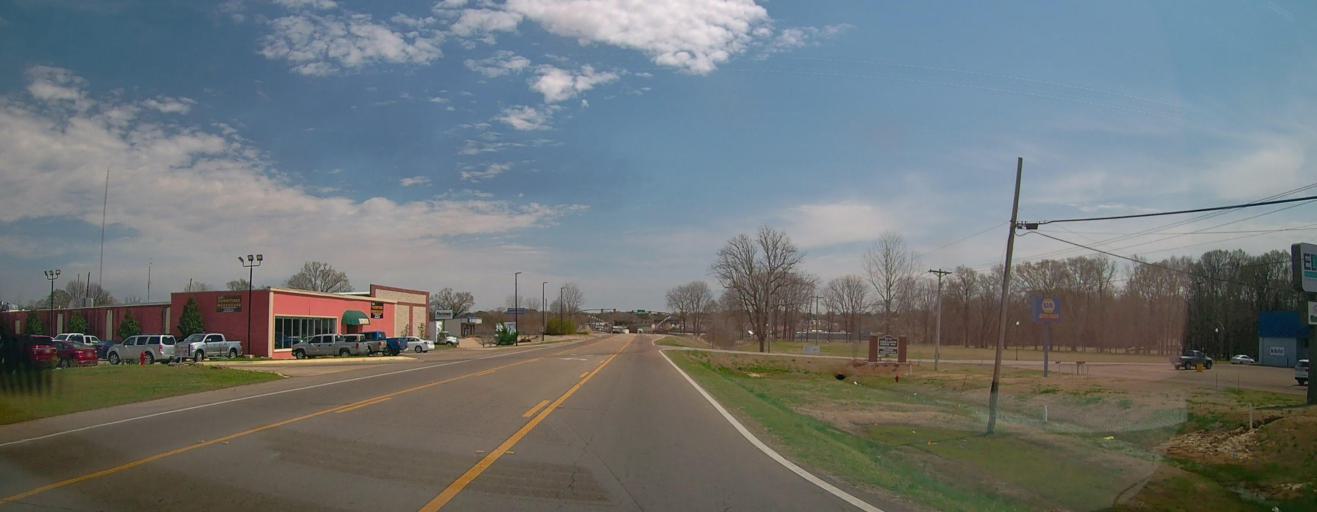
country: US
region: Mississippi
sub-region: Union County
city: New Albany
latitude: 34.4956
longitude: -89.0166
